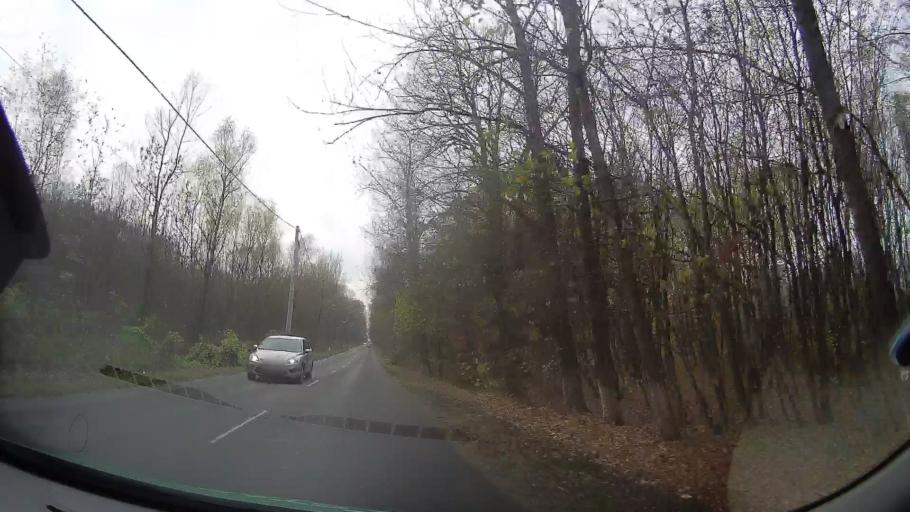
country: RO
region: Ilfov
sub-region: Comuna Snagov
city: Snagov
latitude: 44.7178
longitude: 26.2010
